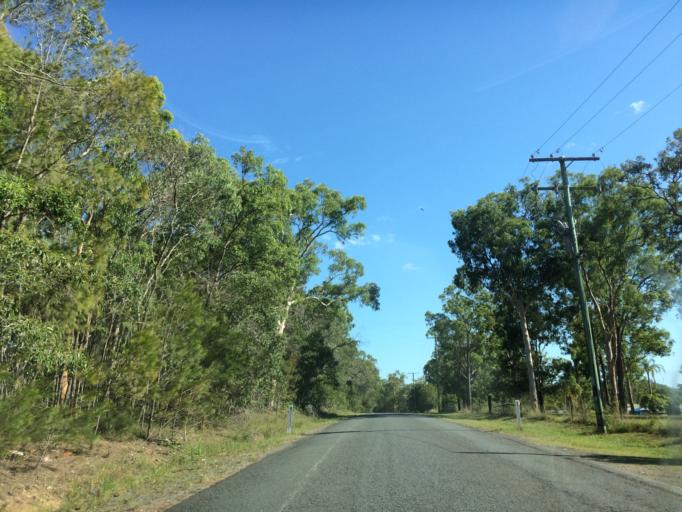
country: AU
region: Queensland
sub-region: Ipswich
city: Springfield Lakes
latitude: -27.7063
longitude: 152.9567
